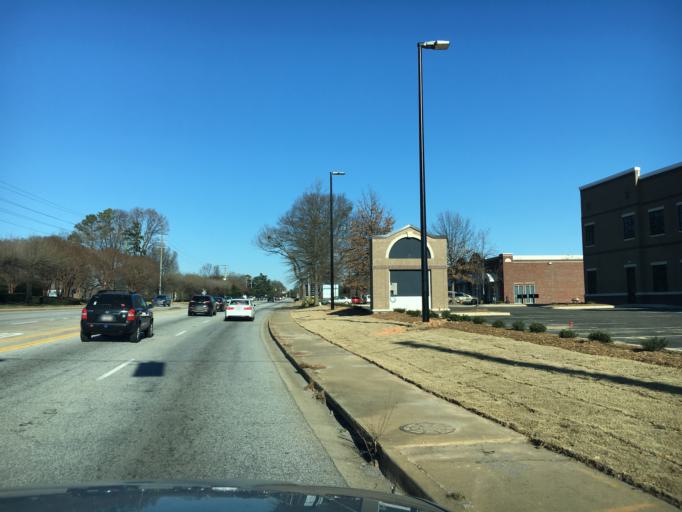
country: US
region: South Carolina
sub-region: Greenville County
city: Mauldin
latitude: 34.8089
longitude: -82.2810
